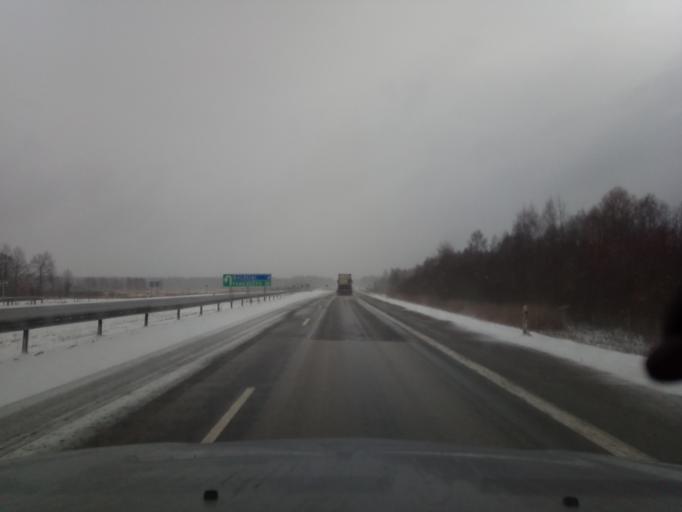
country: LT
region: Vilnius County
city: Ukmerge
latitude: 55.4509
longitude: 24.6696
